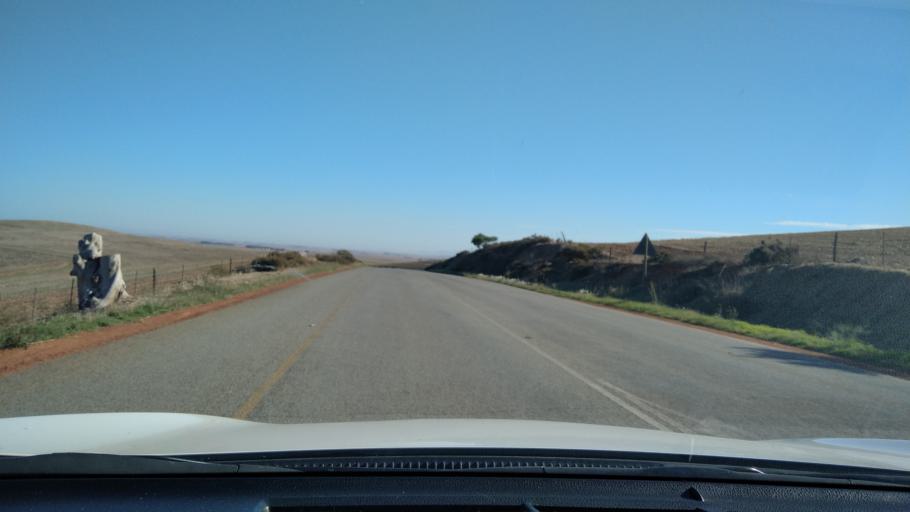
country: ZA
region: Western Cape
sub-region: West Coast District Municipality
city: Malmesbury
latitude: -33.3886
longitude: 18.6713
